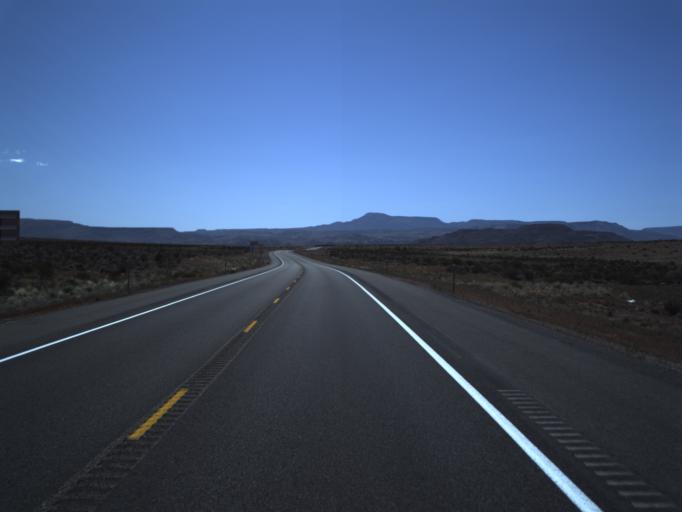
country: US
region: Utah
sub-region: Washington County
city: Washington
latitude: 37.0451
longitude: -113.4857
